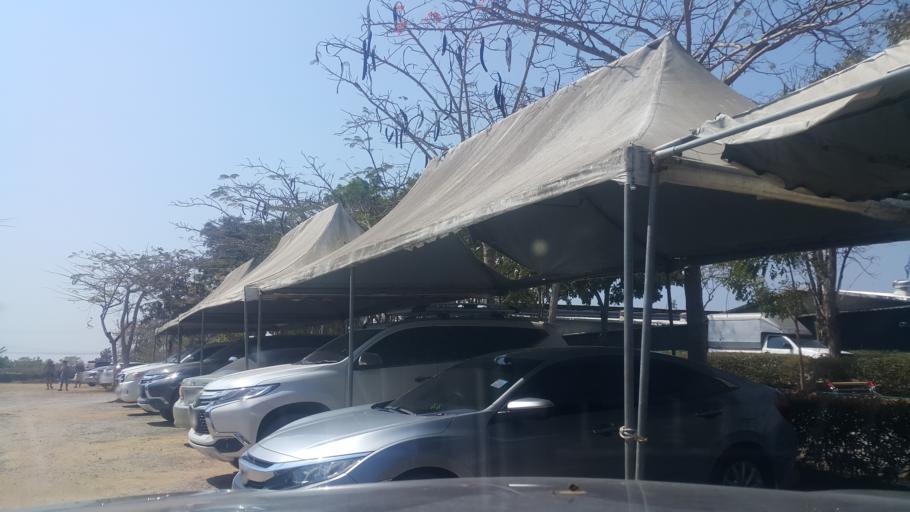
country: TH
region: Nakhon Ratchasima
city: Wang Nam Khiao
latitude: 14.3420
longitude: 101.9442
